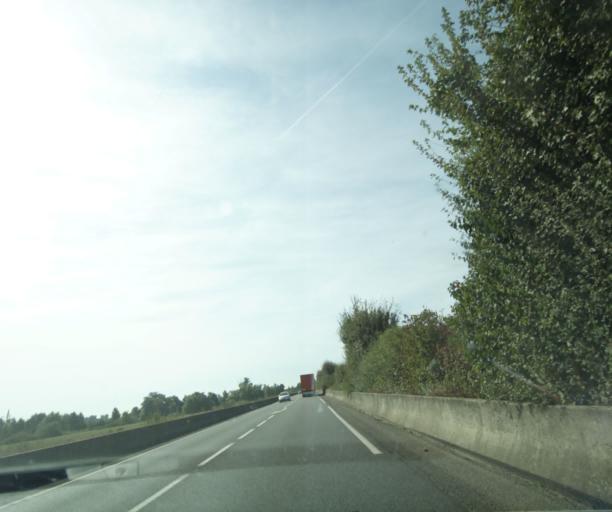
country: FR
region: Auvergne
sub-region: Departement de l'Allier
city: Saint-Remy-en-Rollat
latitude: 46.1884
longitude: 3.4061
